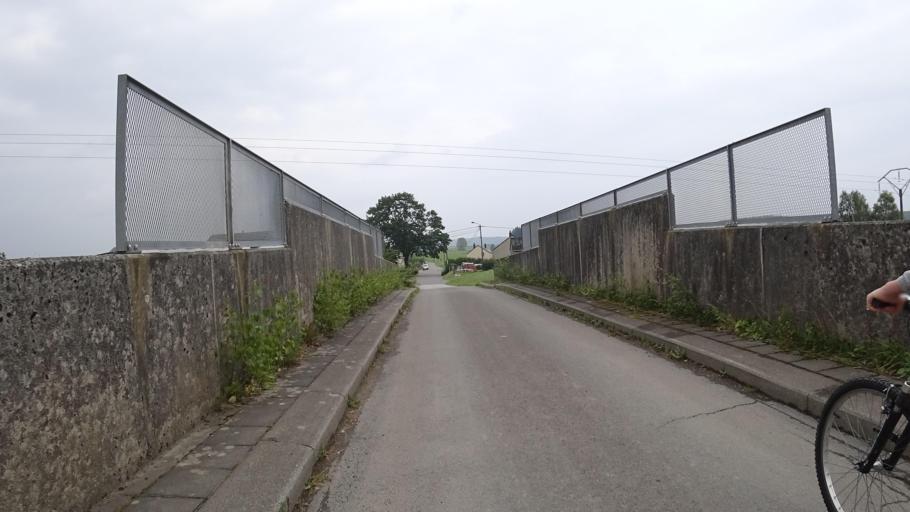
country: BE
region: Wallonia
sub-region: Province du Luxembourg
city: Chiny
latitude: 49.8061
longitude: 5.3268
